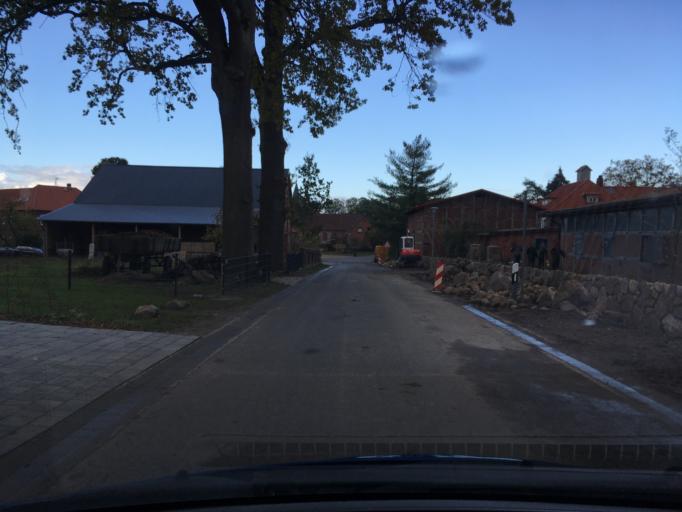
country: DE
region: Lower Saxony
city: Reinstorf
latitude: 53.2498
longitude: 10.5675
